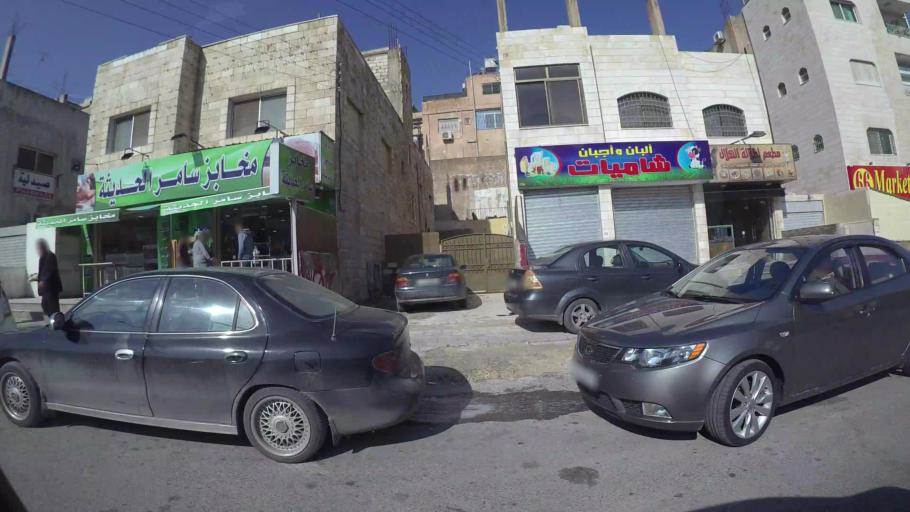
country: JO
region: Amman
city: Amman
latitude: 31.9355
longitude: 35.9092
